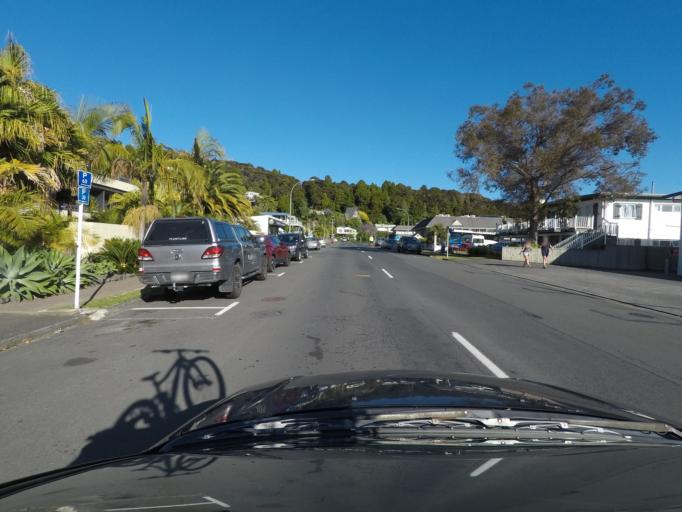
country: NZ
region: Northland
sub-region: Far North District
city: Paihia
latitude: -35.2816
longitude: 174.0904
